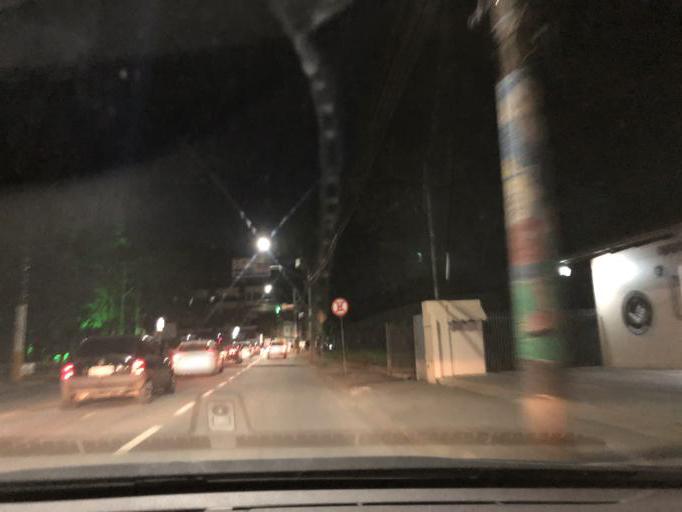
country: BR
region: Santa Catarina
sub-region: Jaragua Do Sul
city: Jaragua do Sul
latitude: -26.4791
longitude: -49.0808
